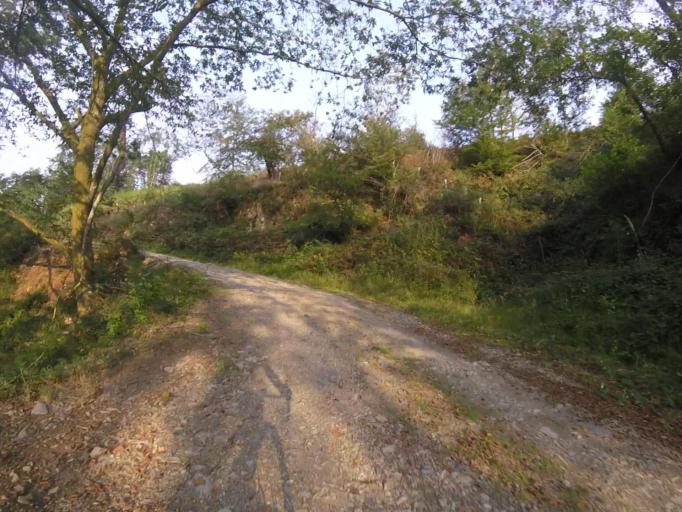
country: ES
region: Navarre
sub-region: Provincia de Navarra
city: Arano
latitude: 43.2510
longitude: -1.8608
